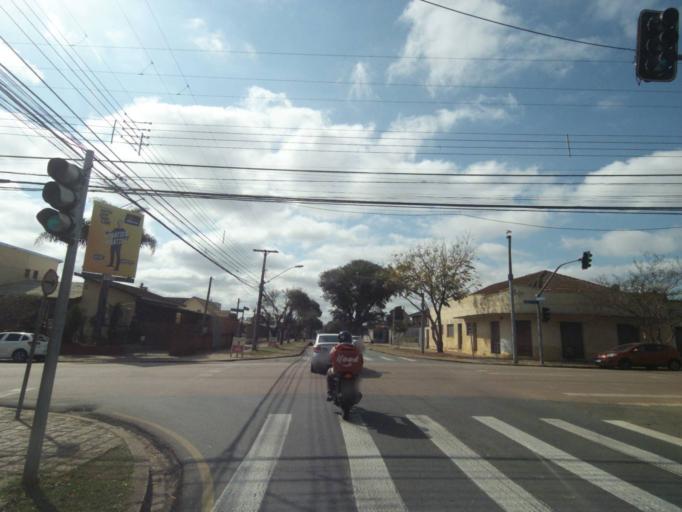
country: BR
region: Parana
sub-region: Curitiba
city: Curitiba
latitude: -25.4523
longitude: -49.2662
